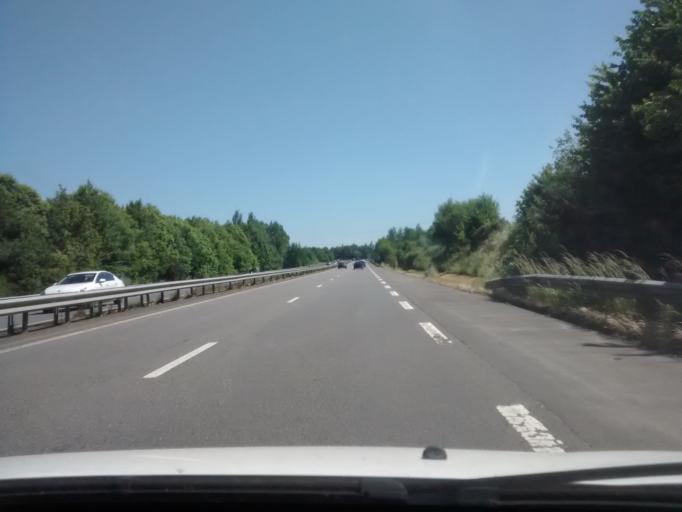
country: FR
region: Brittany
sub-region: Departement d'Ille-et-Vilaine
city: Saint-Domineuc
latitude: 48.3749
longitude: -1.8911
